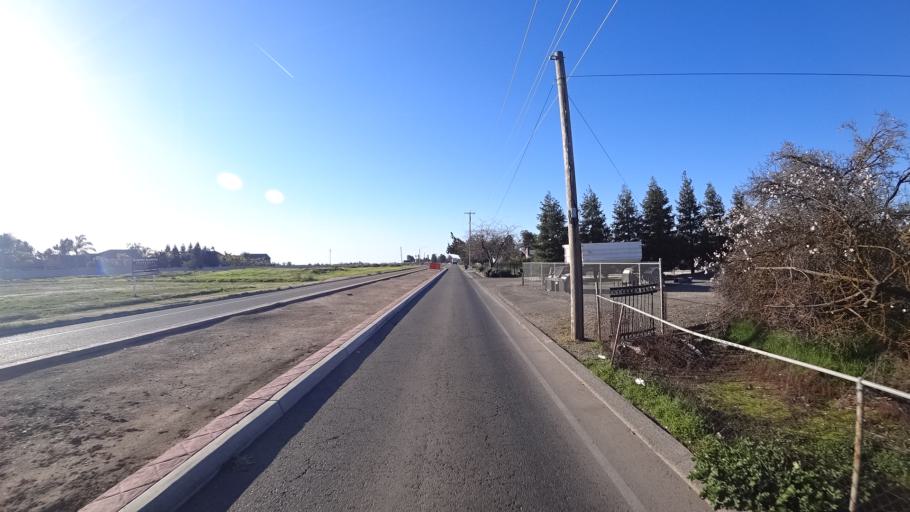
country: US
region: California
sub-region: Fresno County
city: Biola
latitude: 36.8173
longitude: -119.9166
